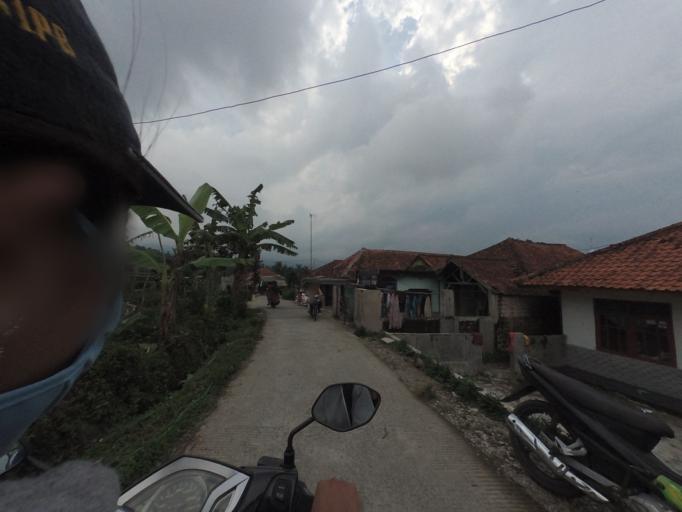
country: ID
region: West Java
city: Ciampea
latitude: -6.6902
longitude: 106.6539
